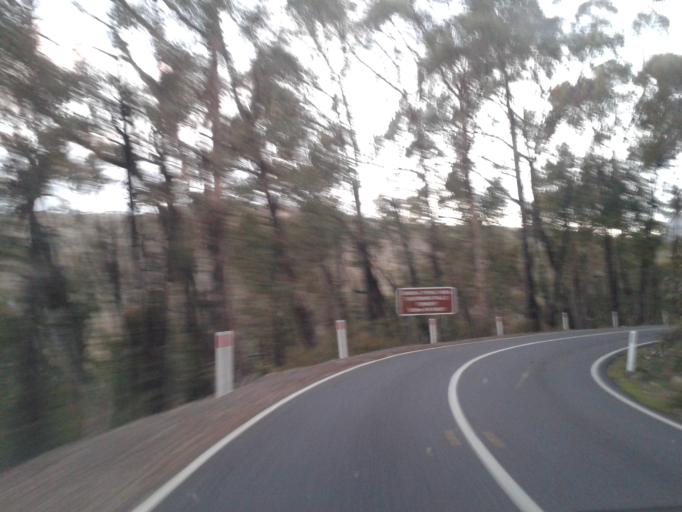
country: AU
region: Victoria
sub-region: Northern Grampians
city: Stawell
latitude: -37.1579
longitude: 142.4966
